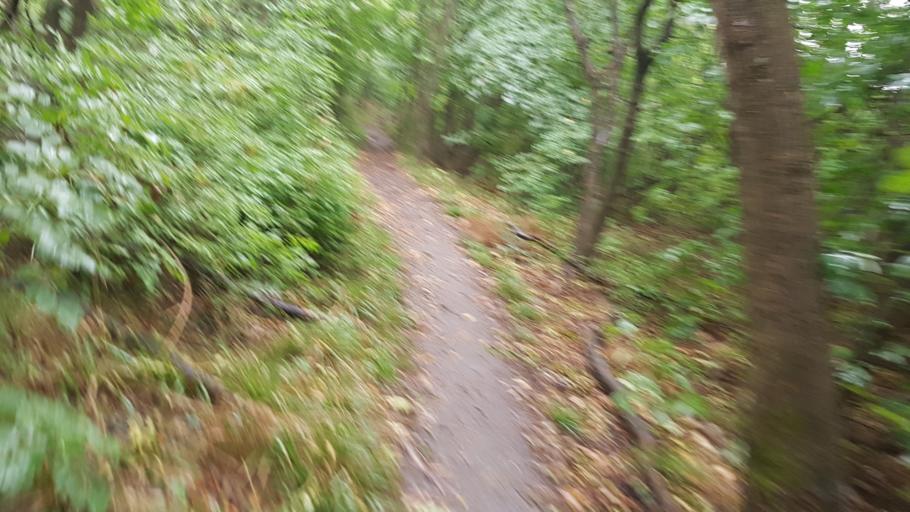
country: HU
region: Pest
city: Toeroekbalint
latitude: 47.4639
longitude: 18.9170
